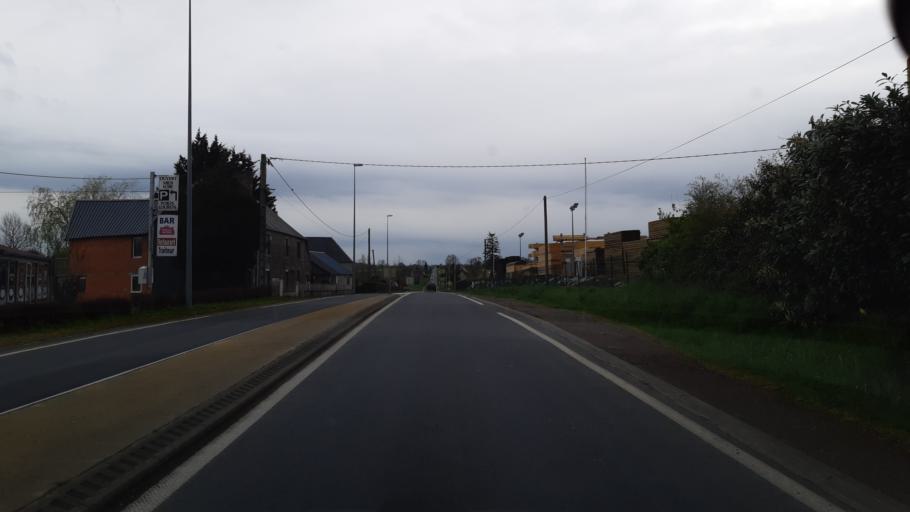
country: FR
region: Lower Normandy
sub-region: Departement de la Manche
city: Percy
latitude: 48.9974
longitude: -1.1546
